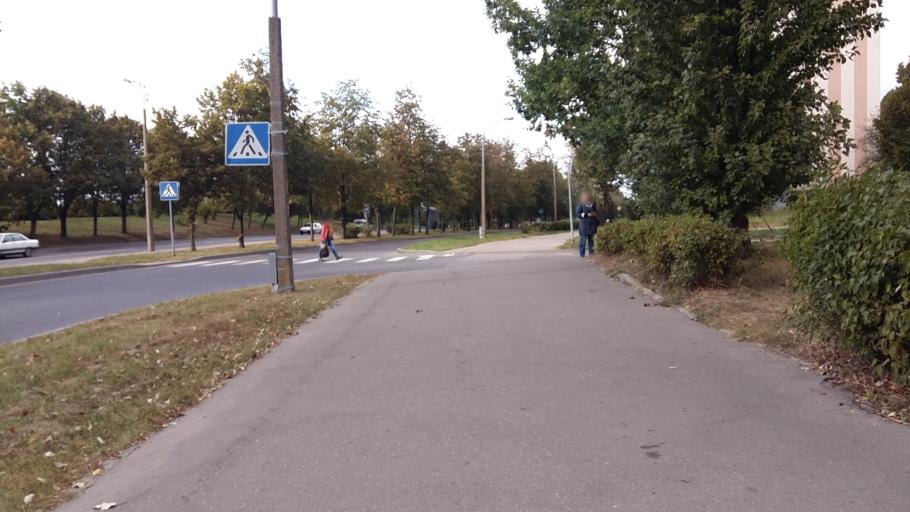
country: BY
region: Grodnenskaya
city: Hrodna
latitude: 53.7016
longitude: 23.7977
